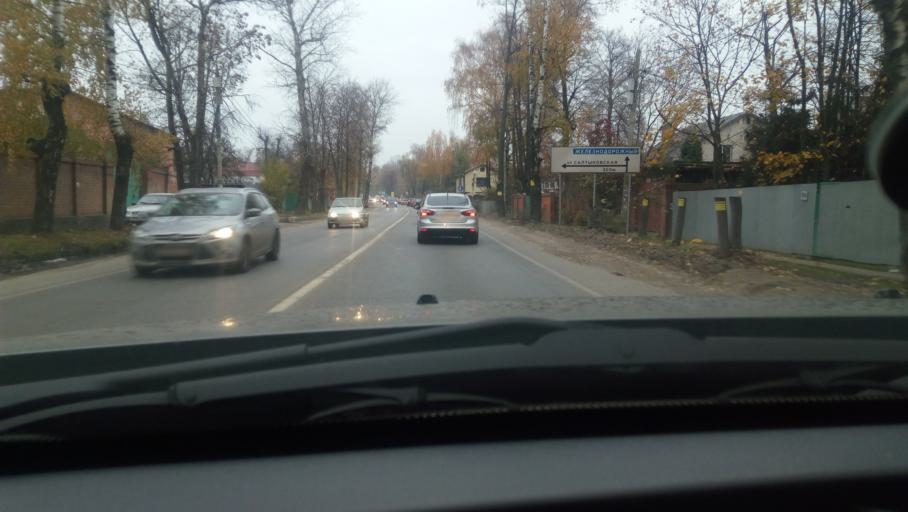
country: RU
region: Moskovskaya
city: Saltykovka
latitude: 55.7522
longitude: 37.9142
